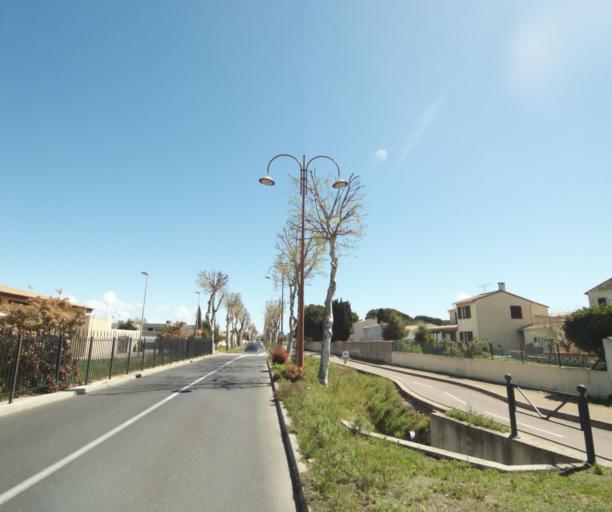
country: FR
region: Languedoc-Roussillon
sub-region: Departement de l'Herault
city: Perols
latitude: 43.5609
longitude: 3.9535
